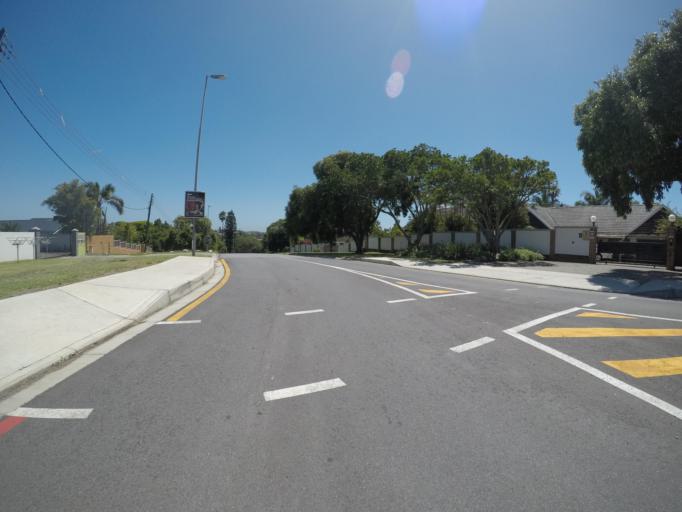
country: ZA
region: Eastern Cape
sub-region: Buffalo City Metropolitan Municipality
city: East London
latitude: -32.9662
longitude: 27.9415
